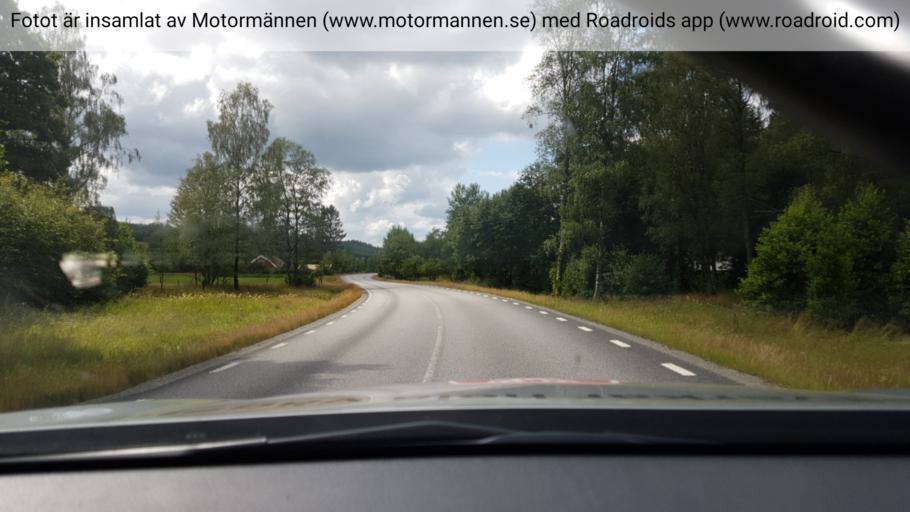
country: SE
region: Vaestra Goetaland
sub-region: Tranemo Kommun
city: Tranemo
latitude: 57.4711
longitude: 13.2454
